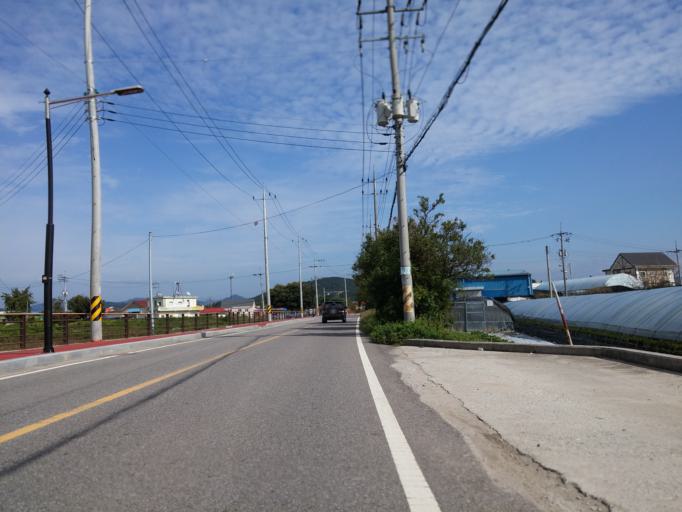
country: KR
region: Chungcheongnam-do
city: Nonsan
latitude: 36.1761
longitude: 127.1349
